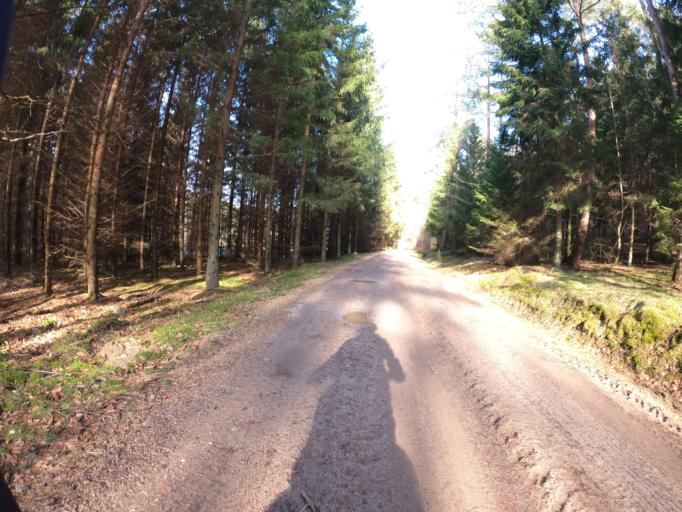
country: PL
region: West Pomeranian Voivodeship
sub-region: Powiat koszalinski
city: Polanow
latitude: 54.2329
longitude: 16.6773
